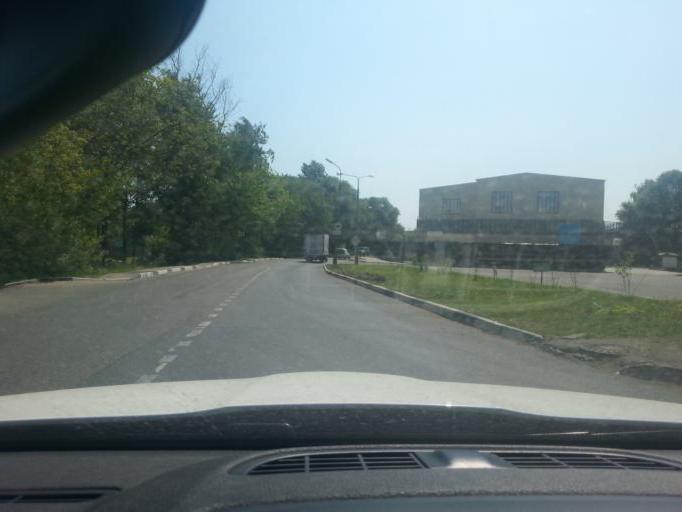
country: RU
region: Moskovskaya
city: Zheleznodorozhnyy
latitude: 55.7300
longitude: 38.0147
